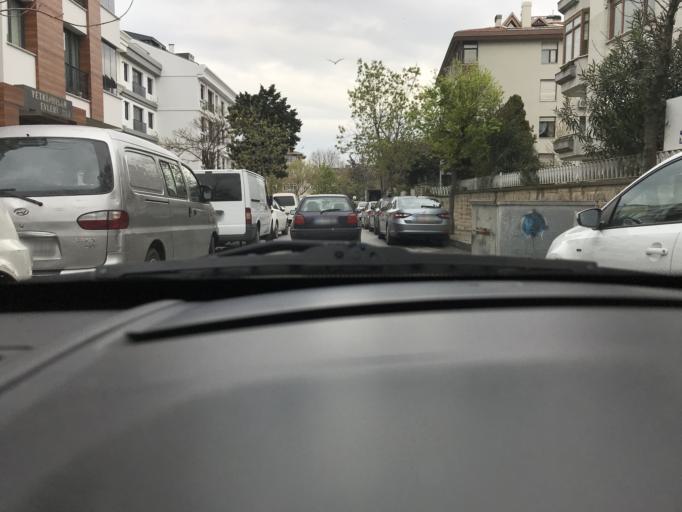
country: TR
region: Istanbul
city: Bahcelievler
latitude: 40.9619
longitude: 28.8189
